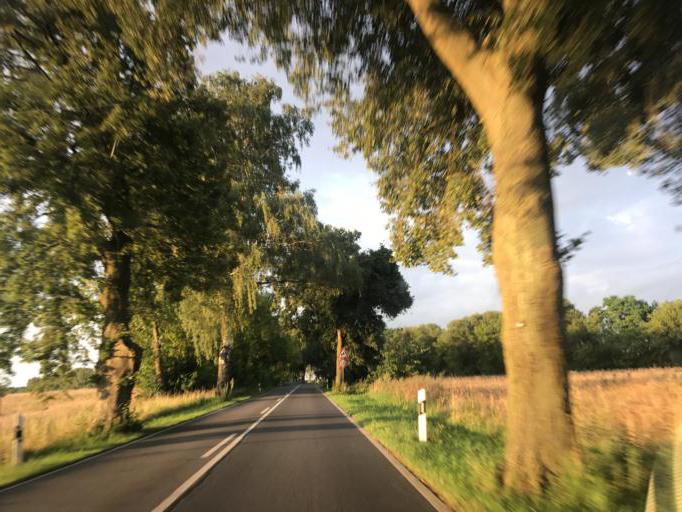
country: DE
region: Mecklenburg-Vorpommern
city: Wesenberg
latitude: 53.3247
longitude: 12.8684
